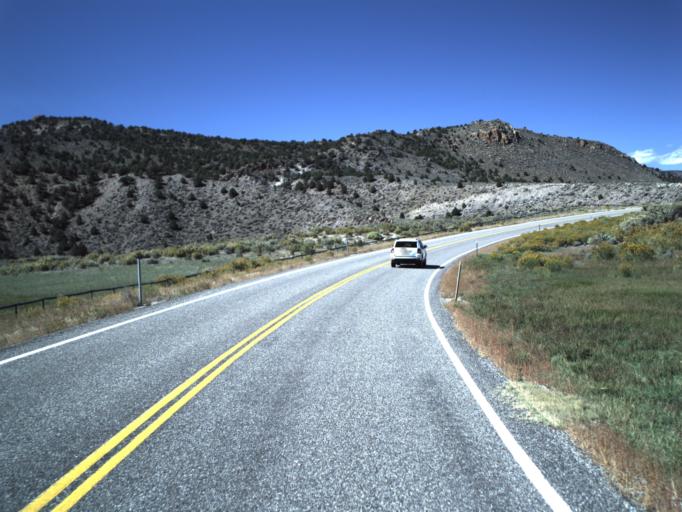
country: US
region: Utah
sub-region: Piute County
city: Junction
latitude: 38.1780
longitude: -112.0762
